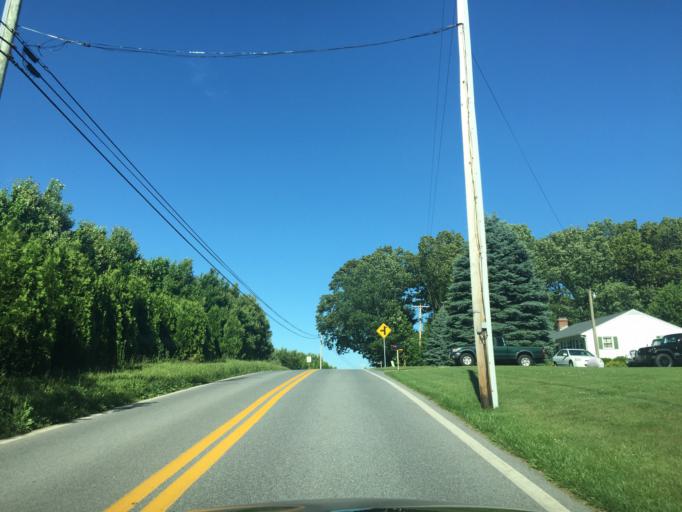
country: US
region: Maryland
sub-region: Carroll County
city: Hampstead
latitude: 39.5607
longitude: -76.9115
